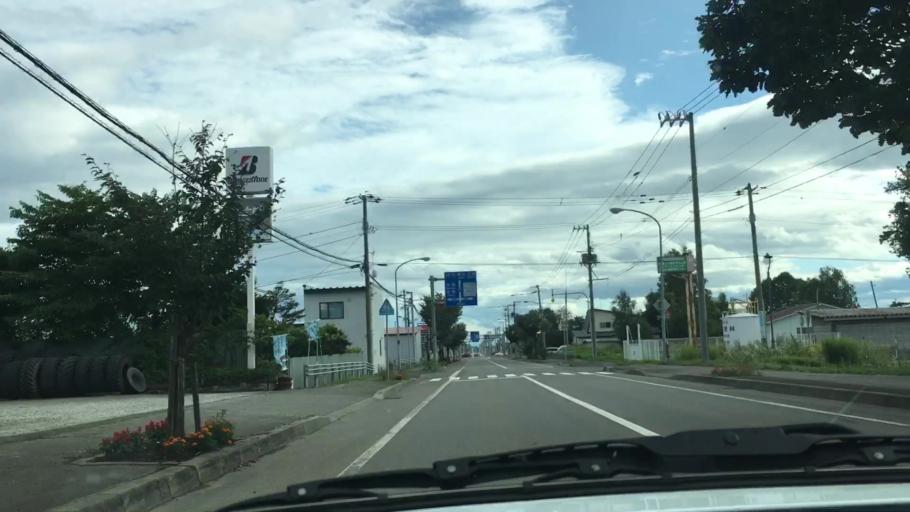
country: JP
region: Hokkaido
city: Otofuke
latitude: 43.2374
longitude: 143.2961
